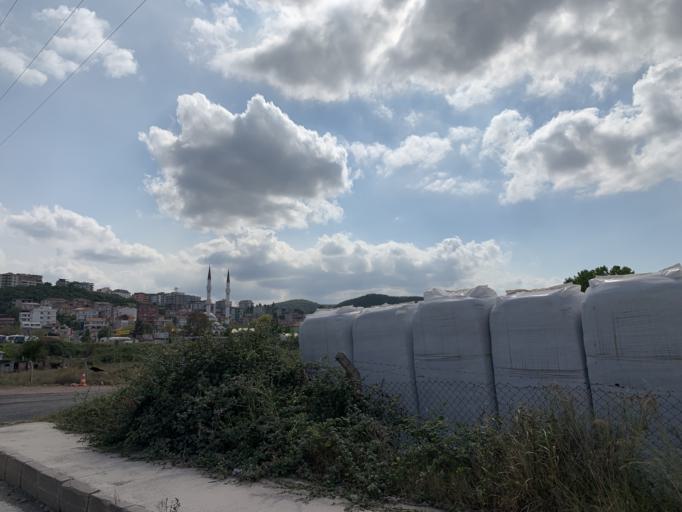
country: TR
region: Yalova
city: Altinova
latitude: 40.6900
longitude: 29.4546
